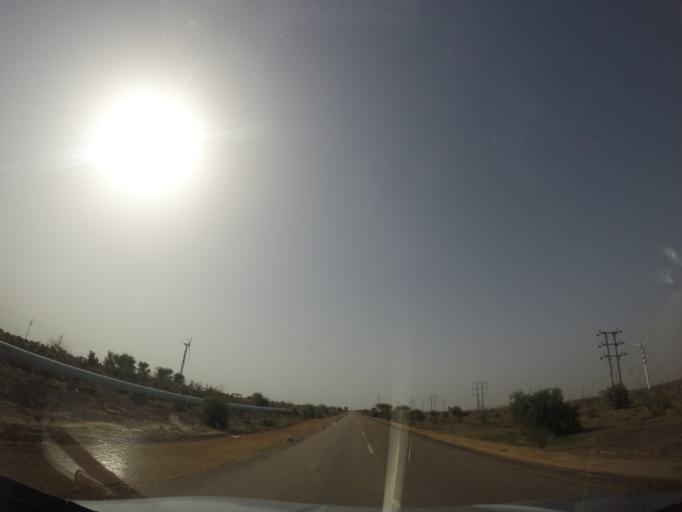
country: IN
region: Rajasthan
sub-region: Jaisalmer
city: Jaisalmer
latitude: 26.7911
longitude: 71.0939
